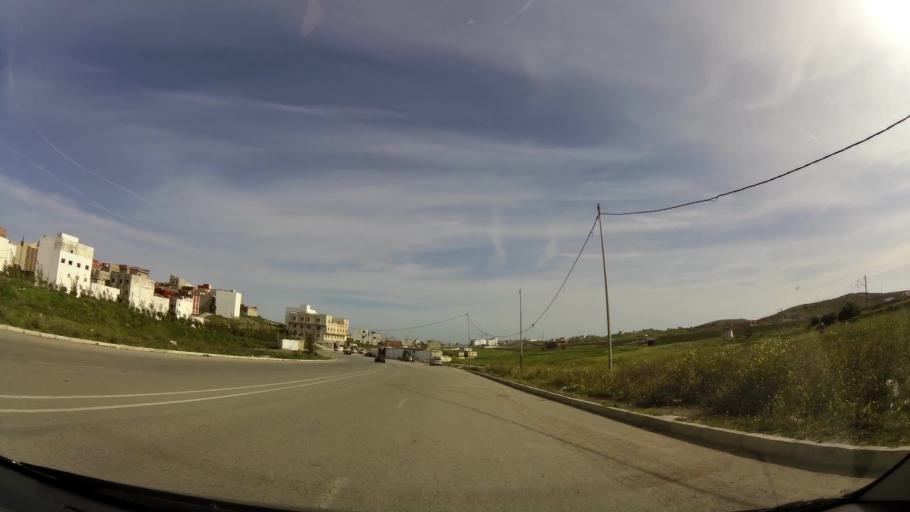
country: MA
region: Tanger-Tetouan
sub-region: Tanger-Assilah
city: Tangier
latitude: 35.7084
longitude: -5.8051
